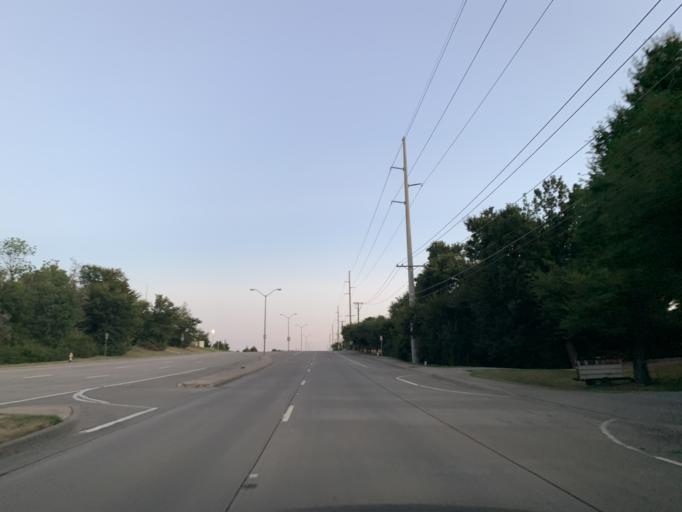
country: US
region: Texas
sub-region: Dallas County
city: Lancaster
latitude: 32.6607
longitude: -96.8057
